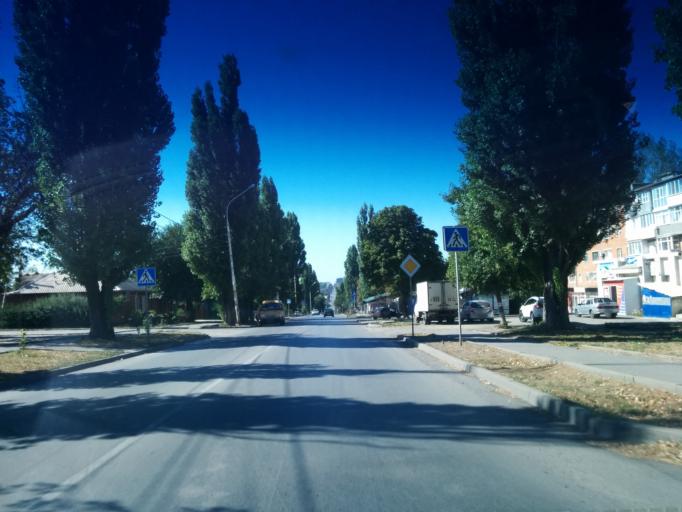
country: RU
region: Rostov
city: Shakhty
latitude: 47.6938
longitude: 40.2467
